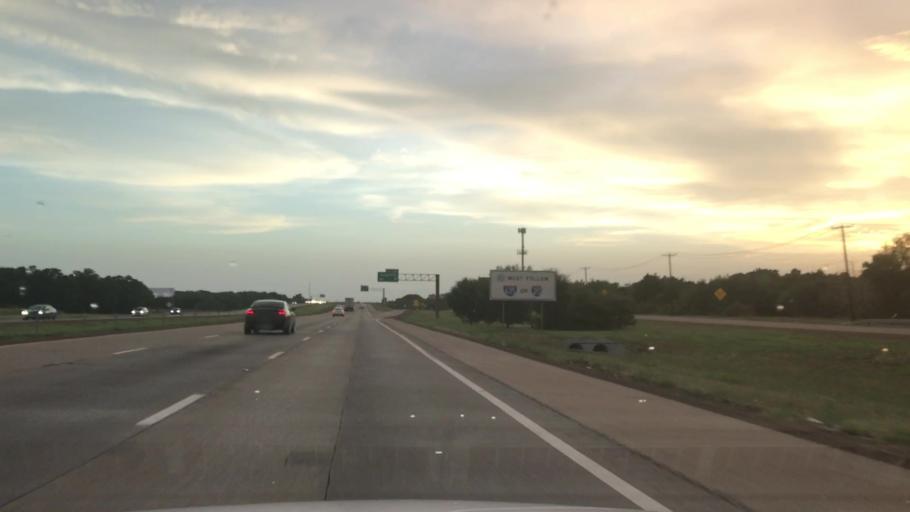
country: US
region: Texas
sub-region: Dallas County
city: Balch Springs
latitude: 32.7034
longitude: -96.5982
